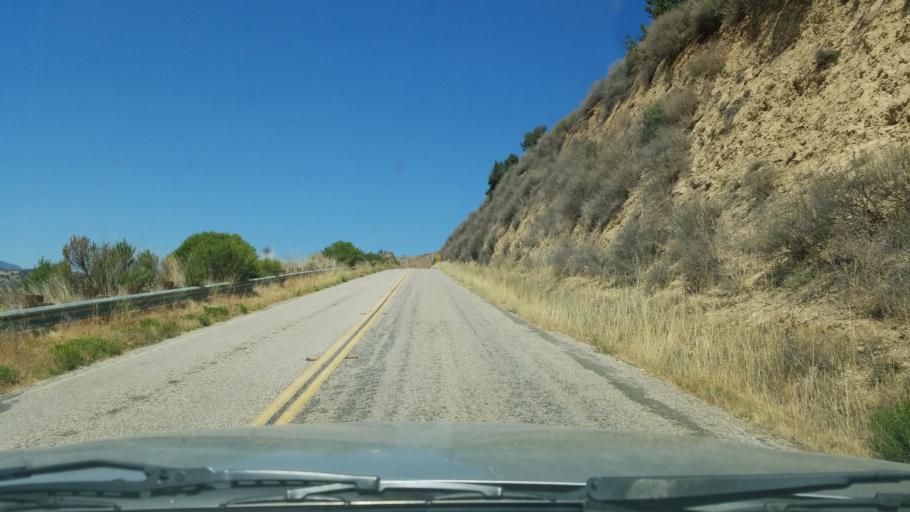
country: US
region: California
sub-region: Monterey County
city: Greenfield
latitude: 36.2717
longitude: -121.3444
